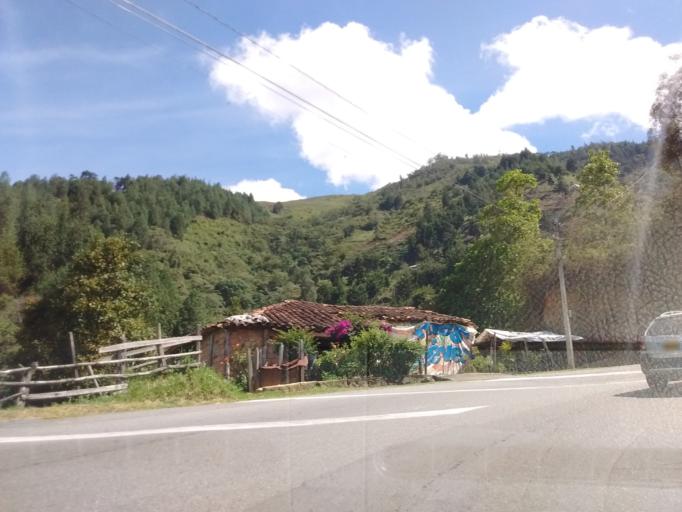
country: CO
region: Antioquia
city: Medellin
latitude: 6.2427
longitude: -75.5179
